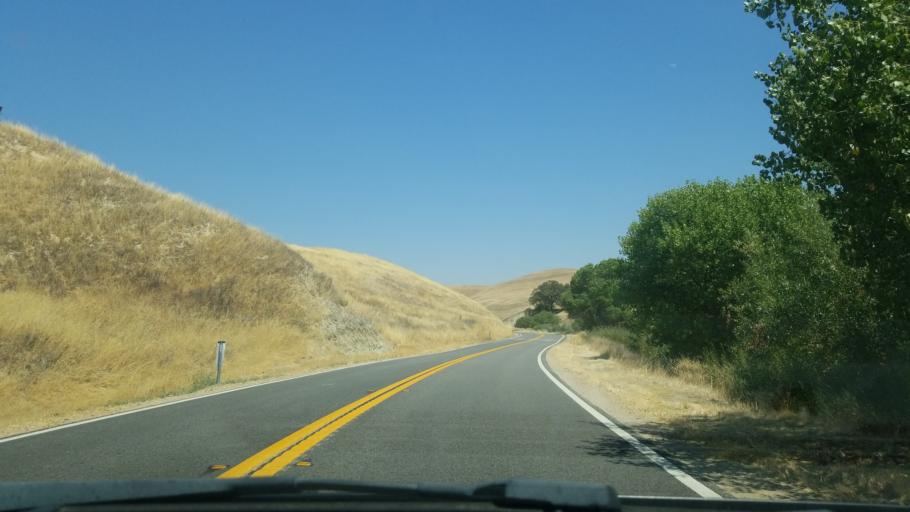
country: US
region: California
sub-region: San Luis Obispo County
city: Shandon
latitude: 35.5776
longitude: -120.4446
